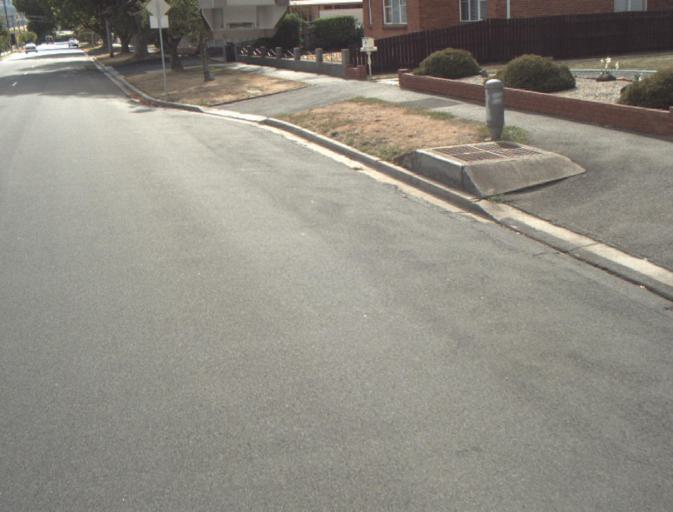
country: AU
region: Tasmania
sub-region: Launceston
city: Newstead
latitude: -41.4557
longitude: 147.1731
